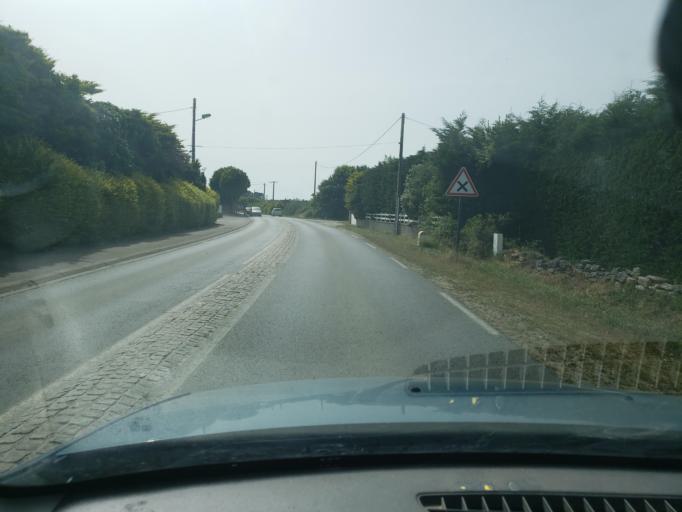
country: FR
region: Brittany
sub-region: Departement du Finistere
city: Plobannalec-Lesconil
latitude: 47.8227
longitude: -4.2356
